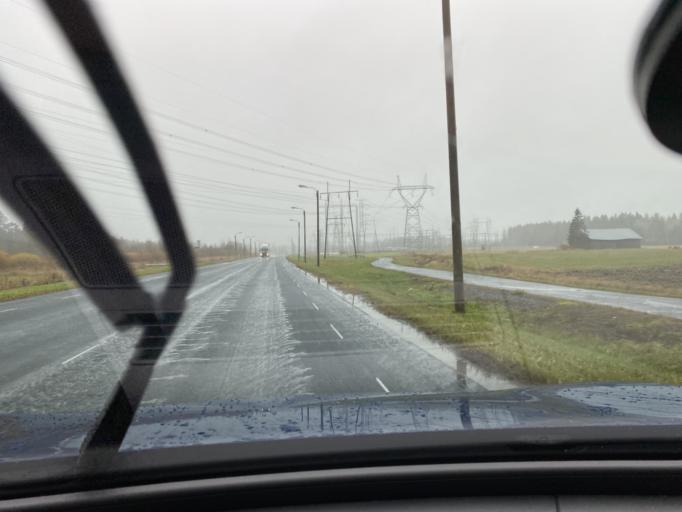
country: FI
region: Haeme
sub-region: Forssa
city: Forssa
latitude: 60.8009
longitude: 23.5844
